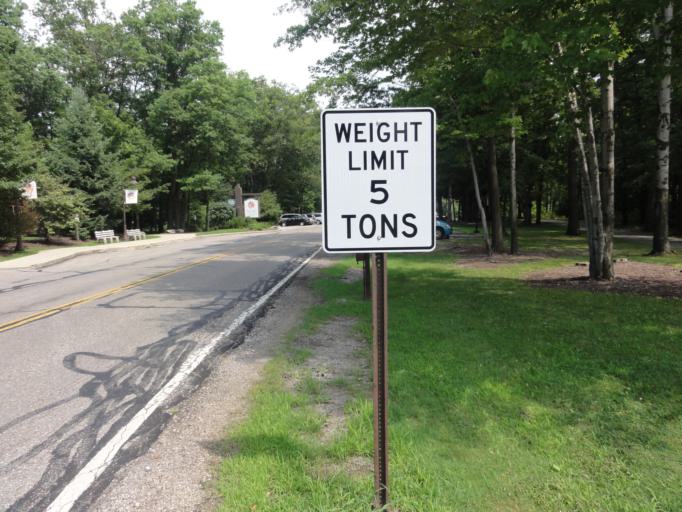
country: US
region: Ohio
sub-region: Cuyahoga County
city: Bay Village
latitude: 41.4853
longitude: -81.9370
